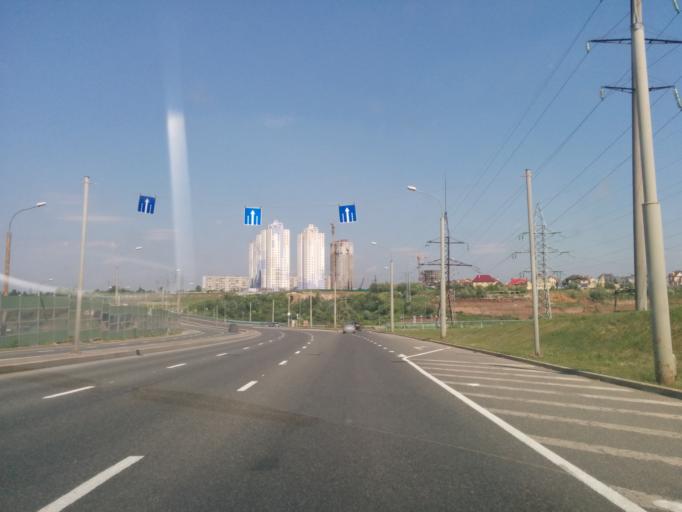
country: RU
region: Perm
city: Perm
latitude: 57.9996
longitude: 56.3135
